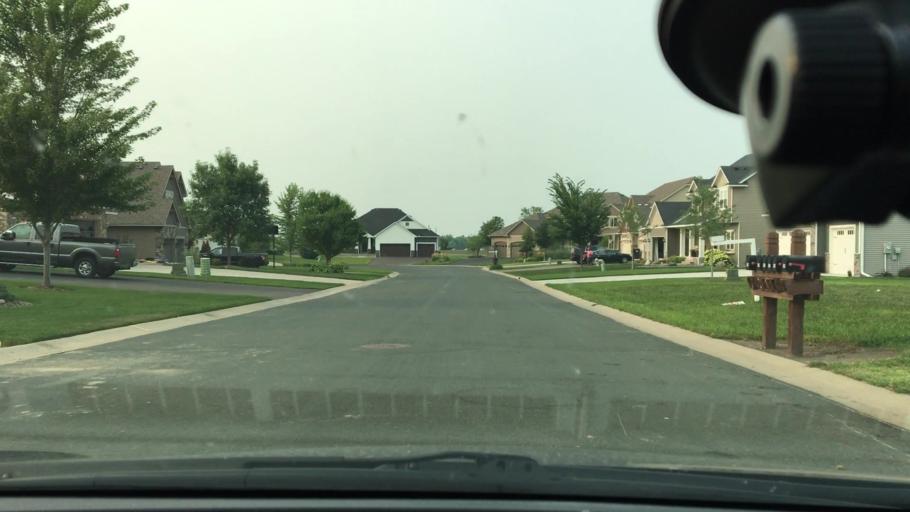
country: US
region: Minnesota
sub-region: Wright County
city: Albertville
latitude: 45.2860
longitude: -93.6803
